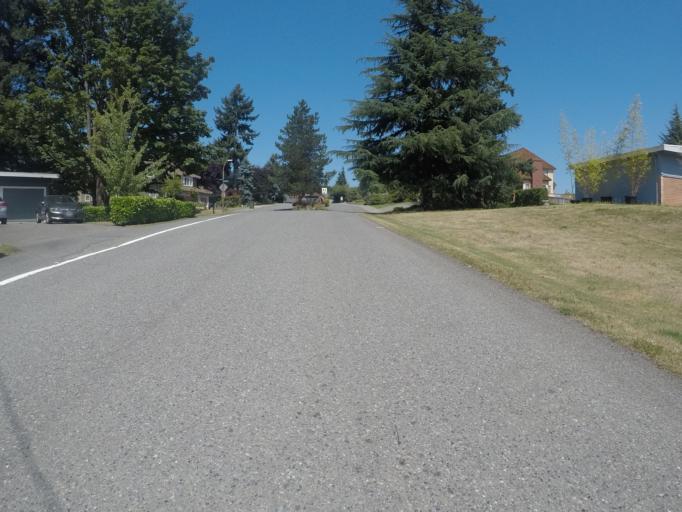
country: US
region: Washington
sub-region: King County
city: Kenmore
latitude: 47.7659
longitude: -122.2571
